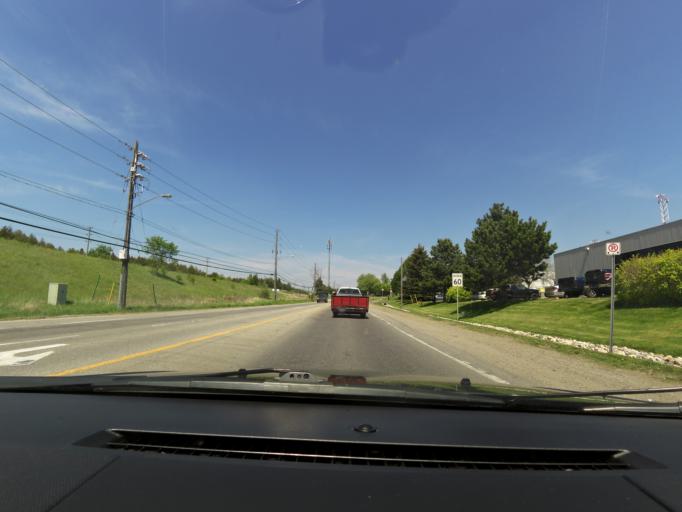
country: CA
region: Ontario
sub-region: Wellington County
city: Guelph
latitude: 43.5626
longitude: -80.2092
